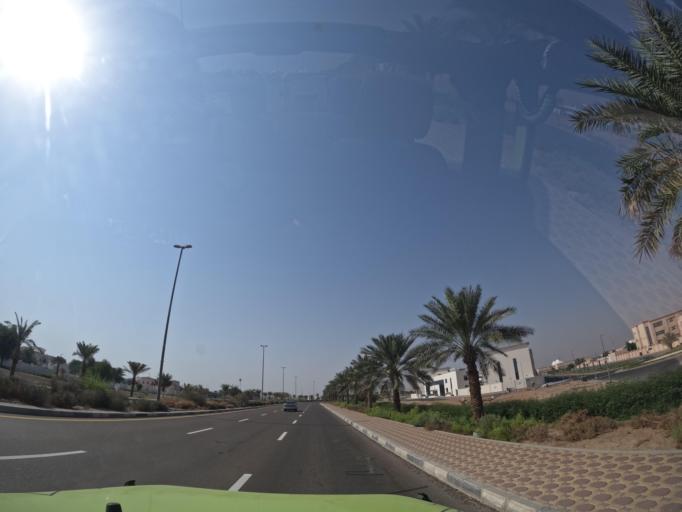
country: AE
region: Abu Dhabi
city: Al Ain
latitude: 24.2596
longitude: 55.6943
